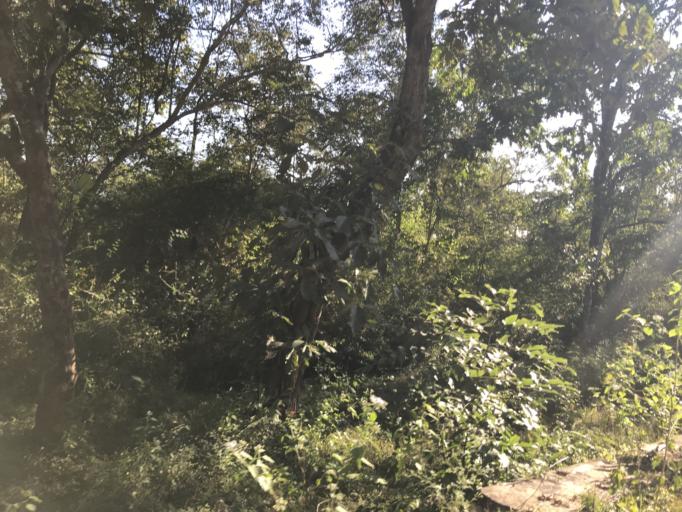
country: IN
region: Karnataka
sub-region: Mysore
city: Heggadadevankote
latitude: 11.9608
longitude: 76.2380
